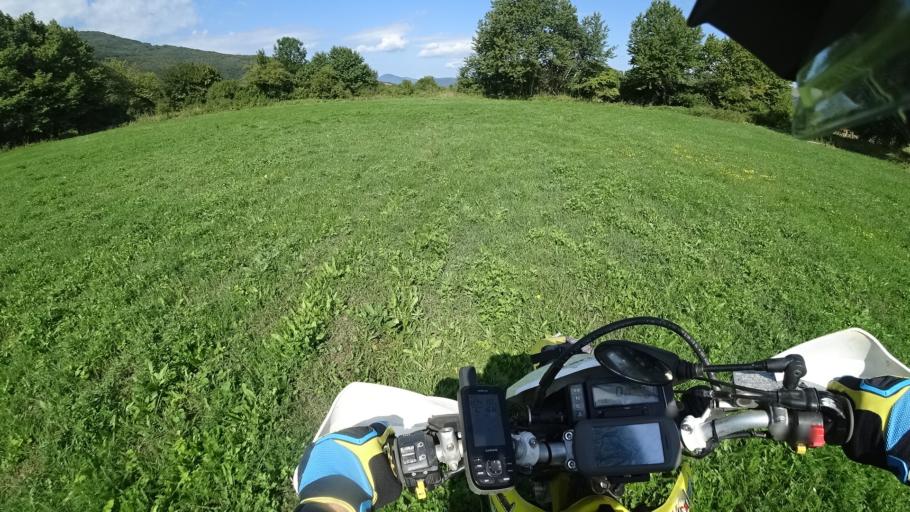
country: HR
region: Zadarska
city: Gracac
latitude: 44.3371
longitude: 15.9511
